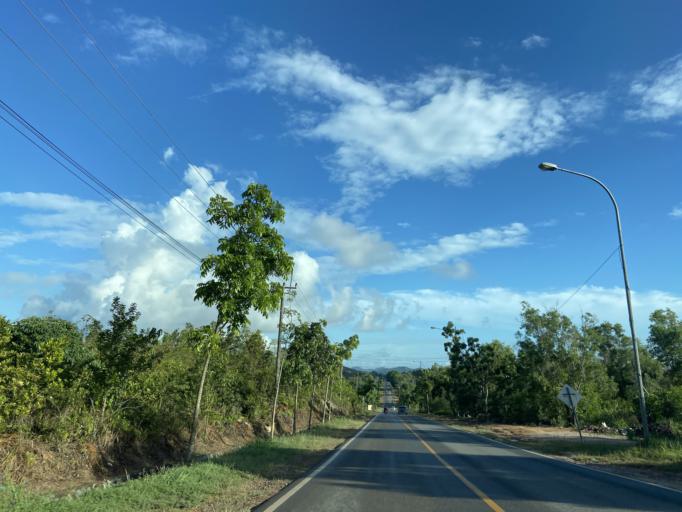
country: SG
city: Singapore
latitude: 1.0137
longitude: 104.0195
